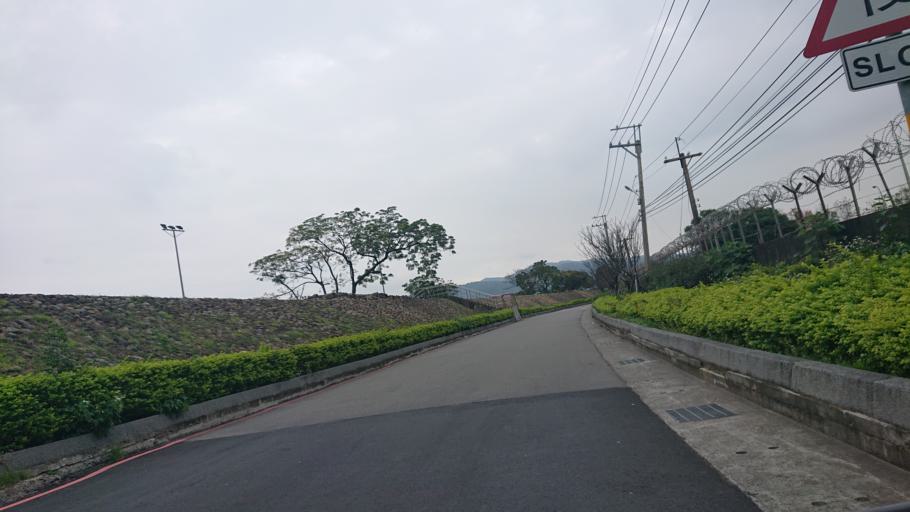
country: TW
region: Taiwan
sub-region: Taoyuan
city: Taoyuan
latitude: 24.9365
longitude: 121.3515
